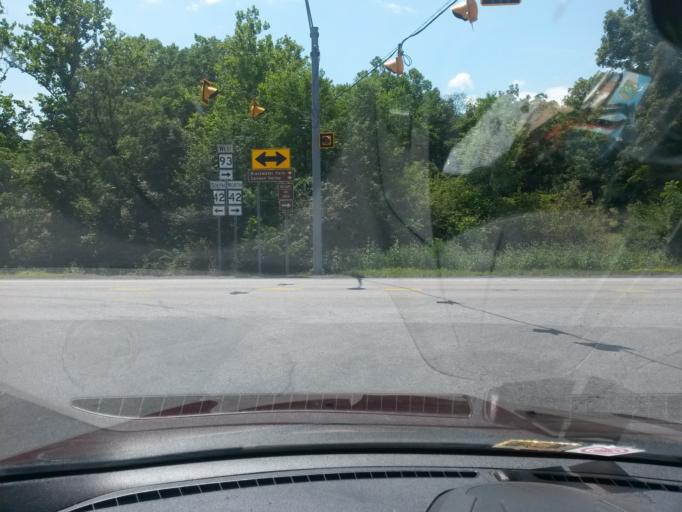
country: US
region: West Virginia
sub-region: Grant County
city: Petersburg
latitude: 39.1922
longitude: -79.1716
